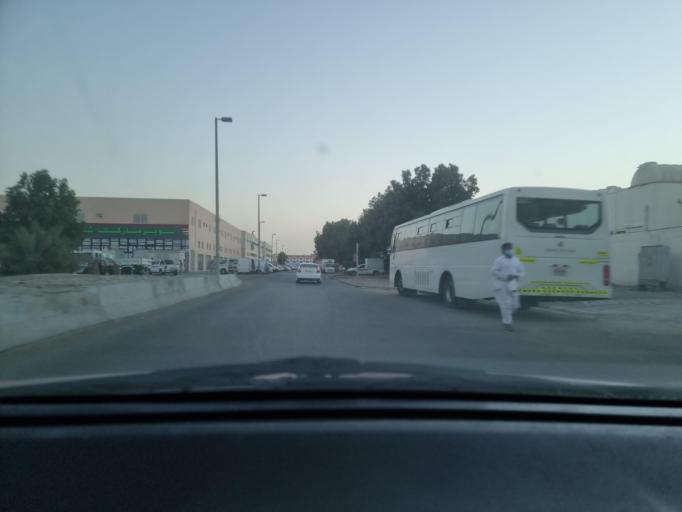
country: AE
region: Abu Dhabi
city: Abu Dhabi
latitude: 24.3520
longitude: 54.5204
